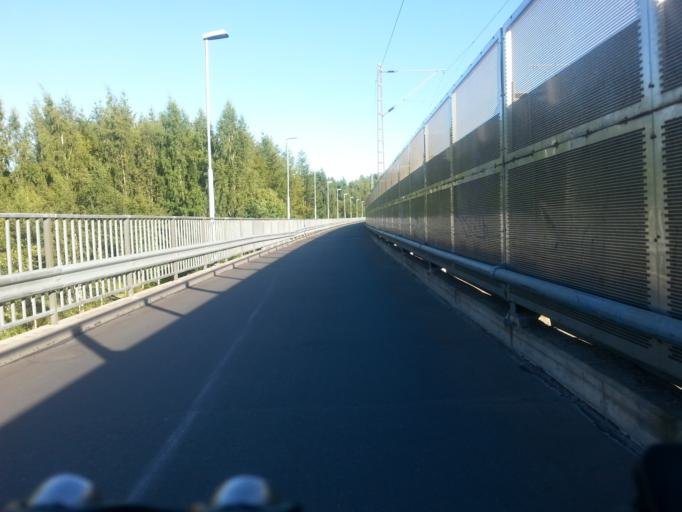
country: FI
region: Uusimaa
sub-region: Helsinki
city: Helsinki
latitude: 60.2148
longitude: 24.9059
